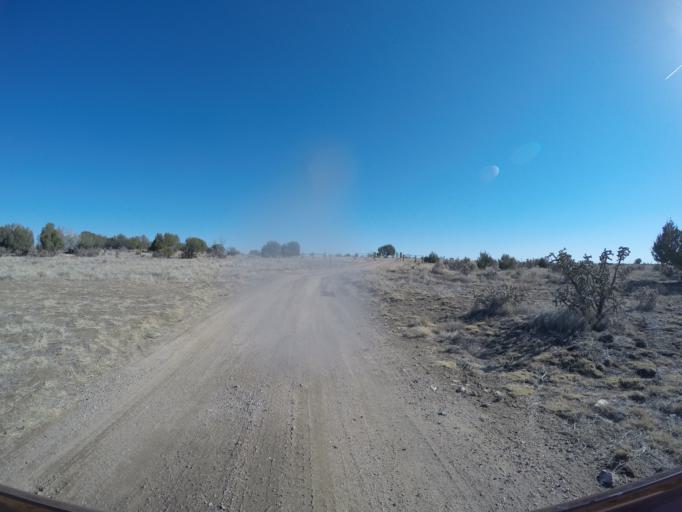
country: US
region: Colorado
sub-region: Otero County
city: La Junta
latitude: 37.6591
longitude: -103.6069
